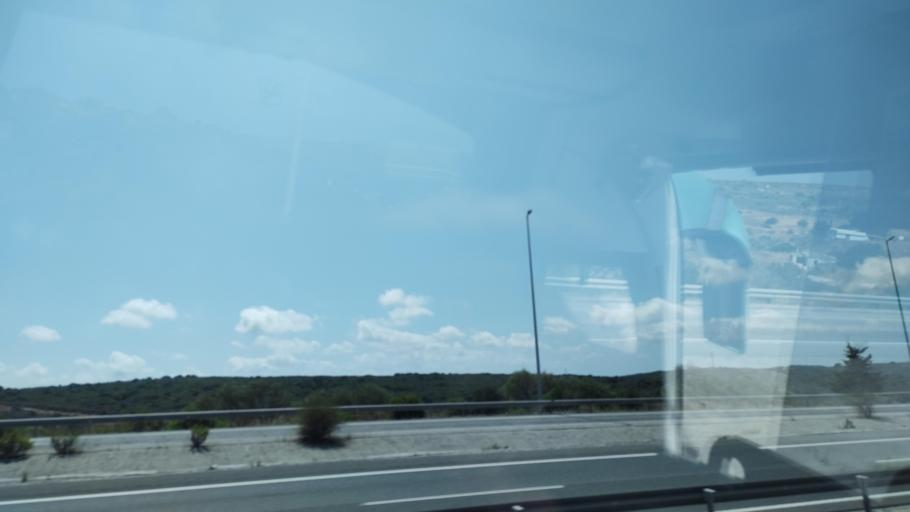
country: ES
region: Andalusia
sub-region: Provincia de Malaga
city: Manilva
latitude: 36.3347
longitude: -5.2681
